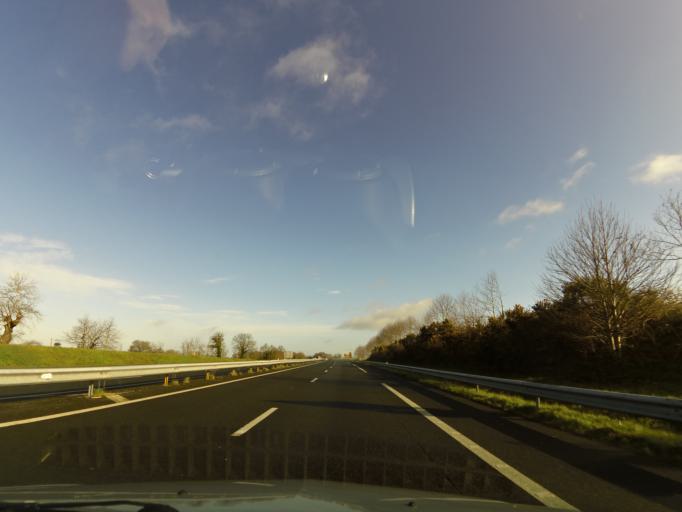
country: FR
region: Brittany
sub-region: Departement d'Ille-et-Vilaine
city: Saint-Etienne-en-Cogles
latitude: 48.4182
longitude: -1.3120
